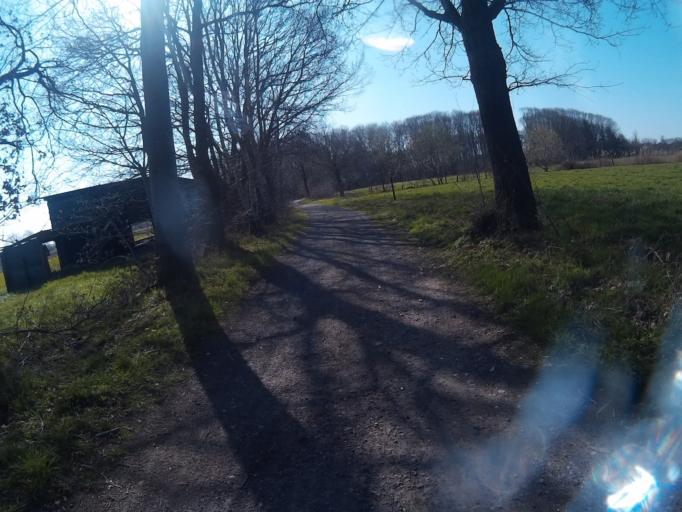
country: BE
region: Flanders
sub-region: Provincie Oost-Vlaanderen
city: Maldegem
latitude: 51.1638
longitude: 3.4655
